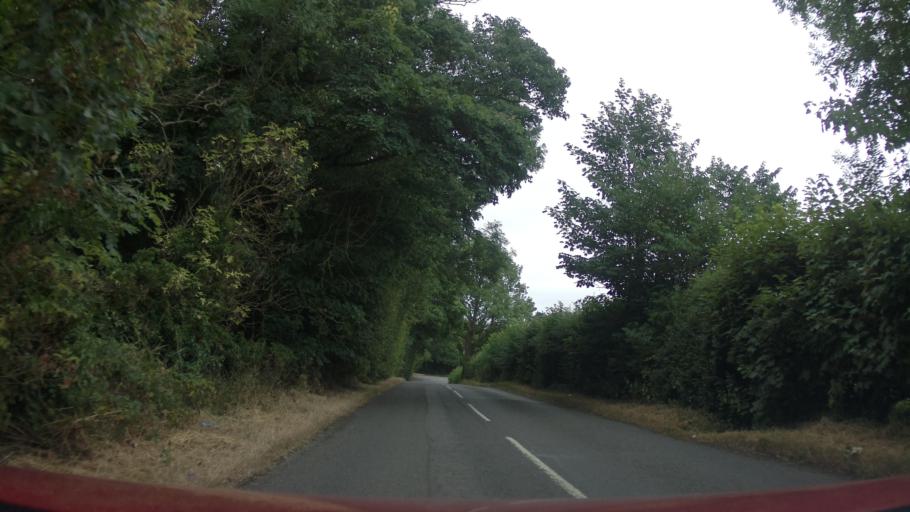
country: GB
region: England
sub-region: Leicestershire
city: Measham
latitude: 52.7298
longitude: -1.5027
